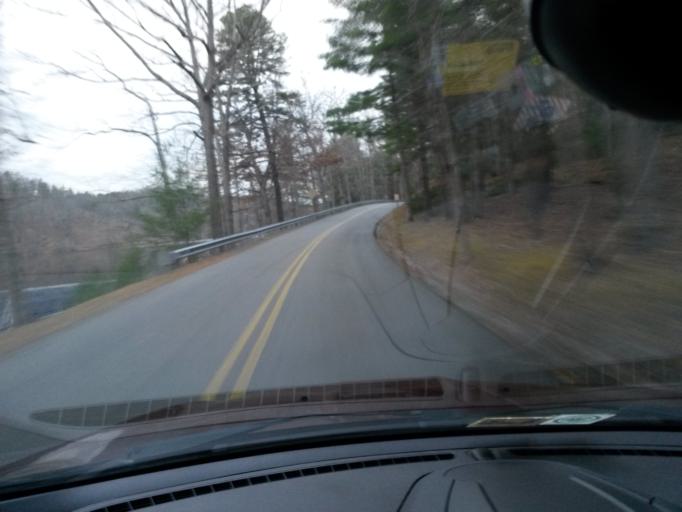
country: US
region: Virginia
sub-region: Alleghany County
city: Clifton Forge
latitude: 37.9024
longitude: -79.8025
